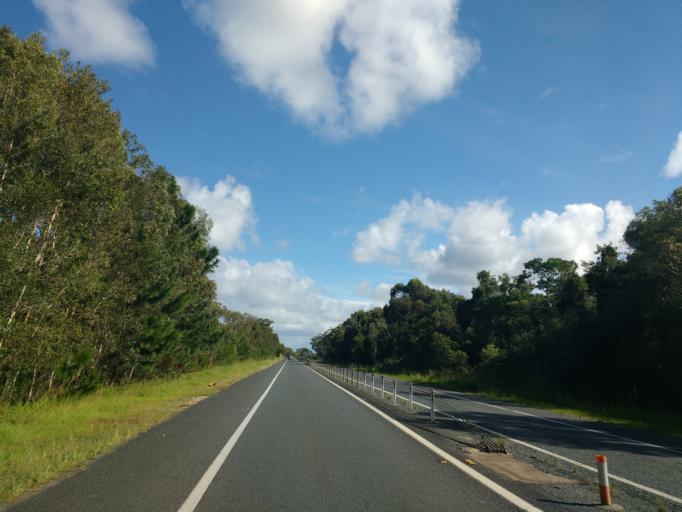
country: AU
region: New South Wales
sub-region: Ballina
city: Ballina
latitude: -28.9311
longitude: 153.4743
